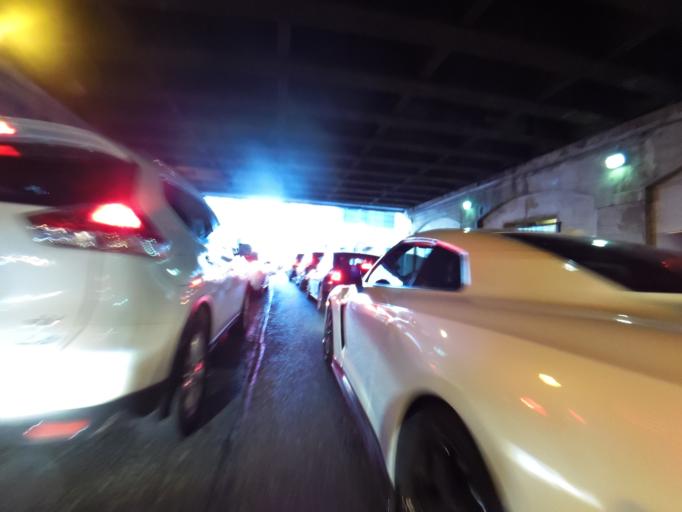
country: CA
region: Ontario
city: Toronto
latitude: 43.6446
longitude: -79.3786
